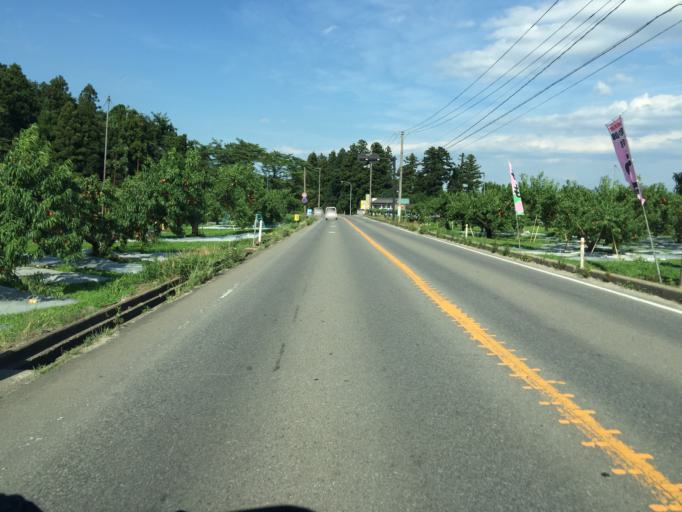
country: JP
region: Fukushima
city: Fukushima-shi
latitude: 37.8136
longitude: 140.4285
